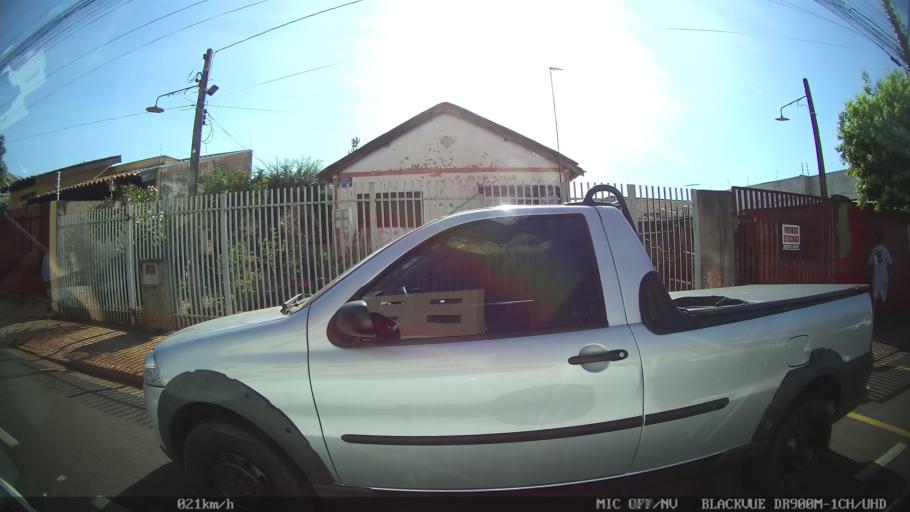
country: BR
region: Sao Paulo
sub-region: Sao Jose Do Rio Preto
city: Sao Jose do Rio Preto
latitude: -20.8024
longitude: -49.3889
